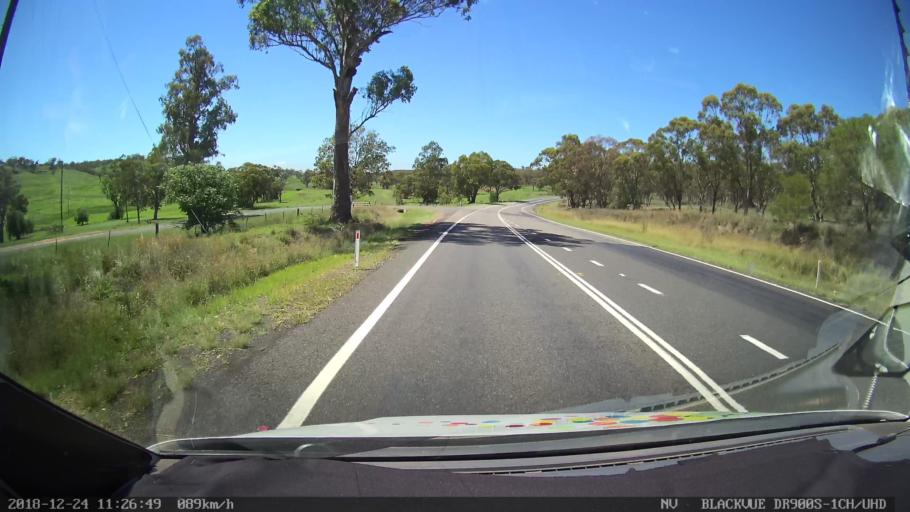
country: AU
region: New South Wales
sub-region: Upper Hunter Shire
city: Merriwa
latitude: -32.1739
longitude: 150.4334
